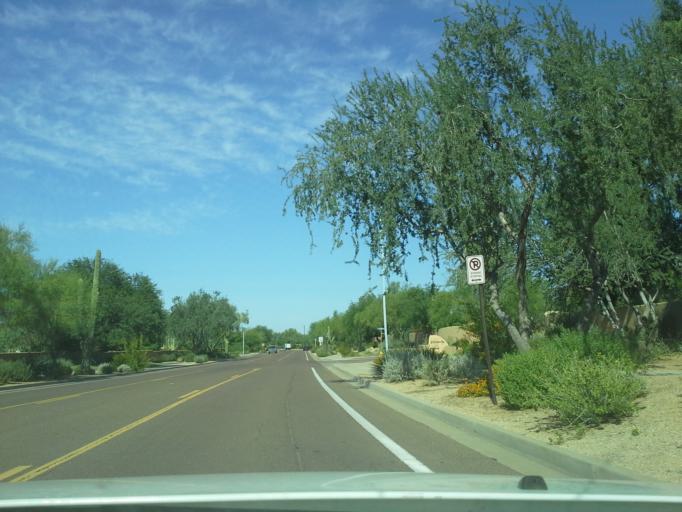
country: US
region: Arizona
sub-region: Maricopa County
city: Carefree
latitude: 33.6761
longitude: -111.9162
